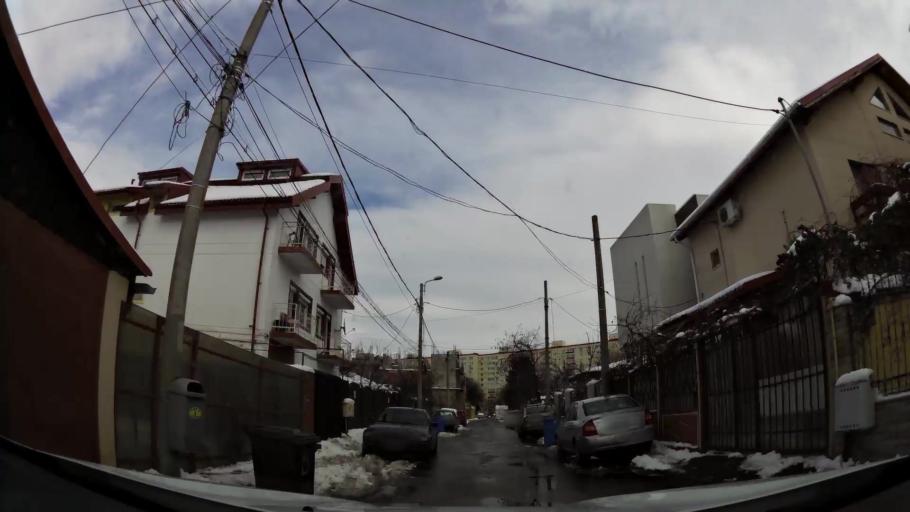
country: RO
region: Bucuresti
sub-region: Municipiul Bucuresti
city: Bucuresti
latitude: 44.3856
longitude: 26.1128
